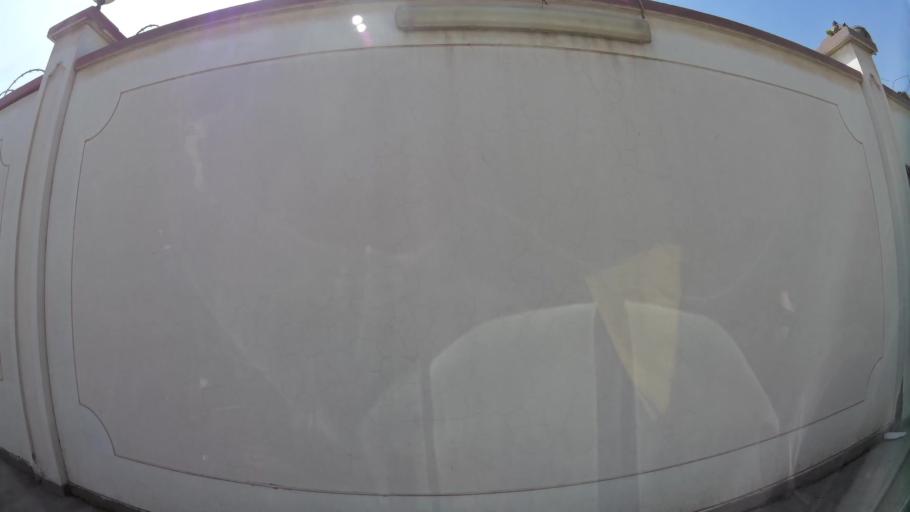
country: BH
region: Northern
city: Madinat `Isa
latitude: 26.1933
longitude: 50.4577
